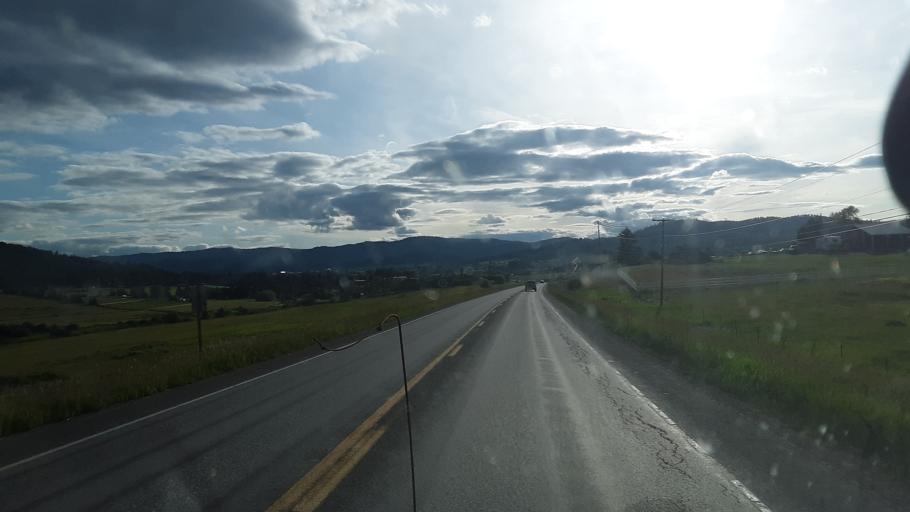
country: US
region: Montana
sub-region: Flathead County
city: Kalispell
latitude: 48.1968
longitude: -114.3595
